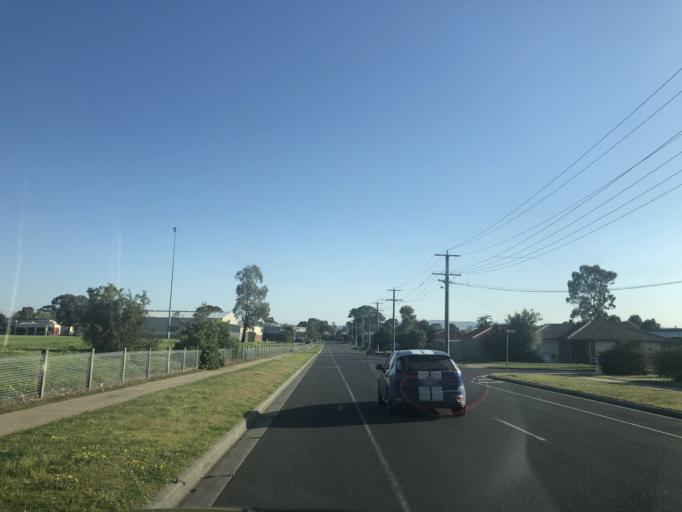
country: AU
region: Victoria
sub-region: Casey
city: Hampton Park
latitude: -38.0380
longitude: 145.2603
